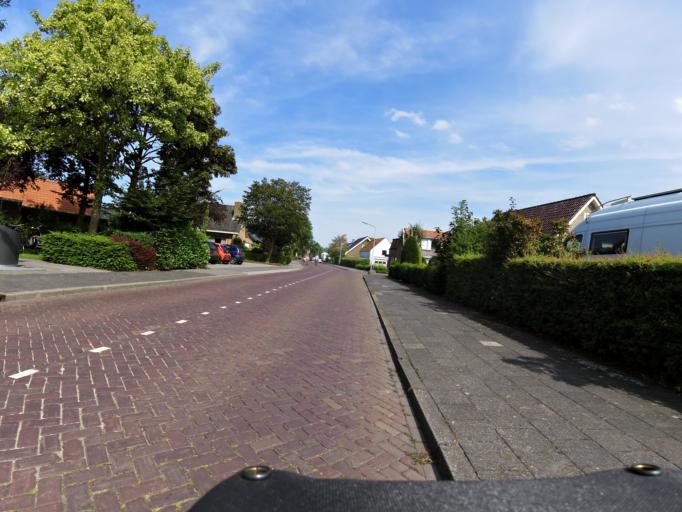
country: NL
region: South Holland
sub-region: Gemeente Goeree-Overflakkee
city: Middelharnis
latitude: 51.7563
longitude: 4.1646
